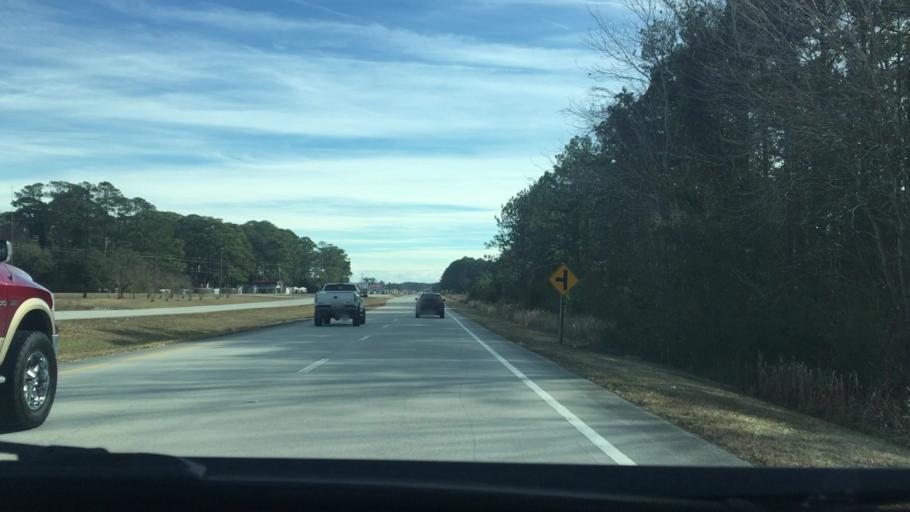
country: US
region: North Carolina
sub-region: Carteret County
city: Newport
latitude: 34.7621
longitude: -76.8548
